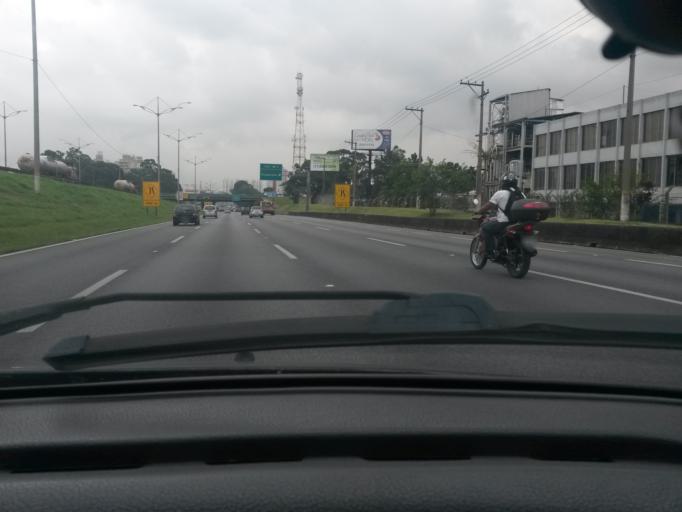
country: BR
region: Sao Paulo
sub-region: Sao Bernardo Do Campo
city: Sao Bernardo do Campo
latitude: -23.6868
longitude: -46.5662
